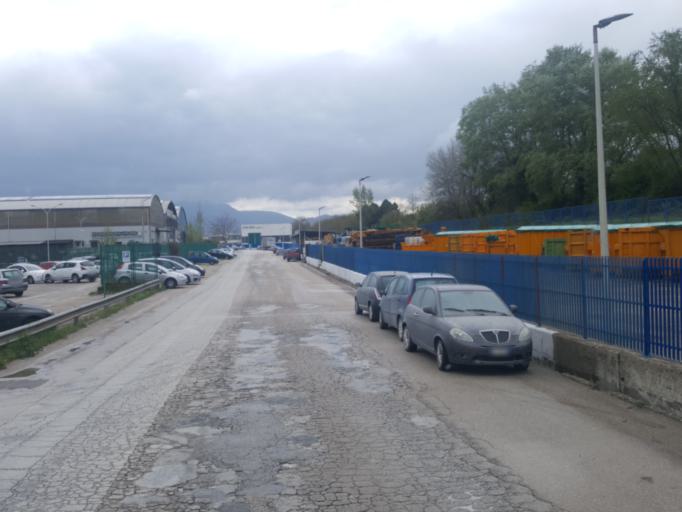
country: IT
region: Campania
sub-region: Provincia di Avellino
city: Atripalda
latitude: 40.9362
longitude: 14.8209
